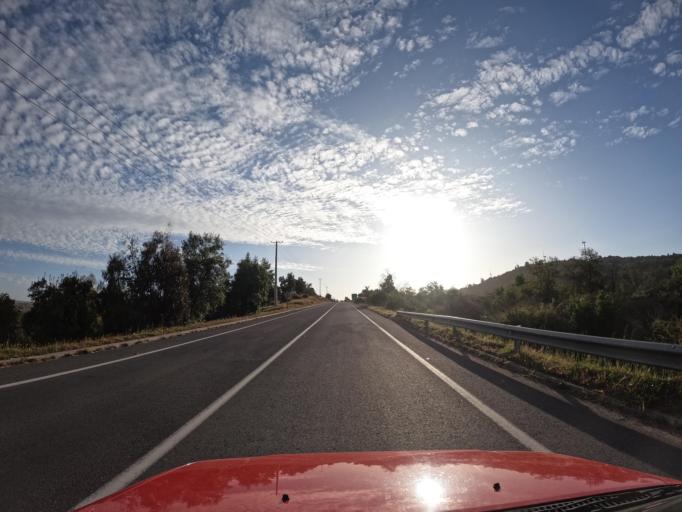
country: CL
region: Valparaiso
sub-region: San Antonio Province
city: San Antonio
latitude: -34.0495
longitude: -71.5951
